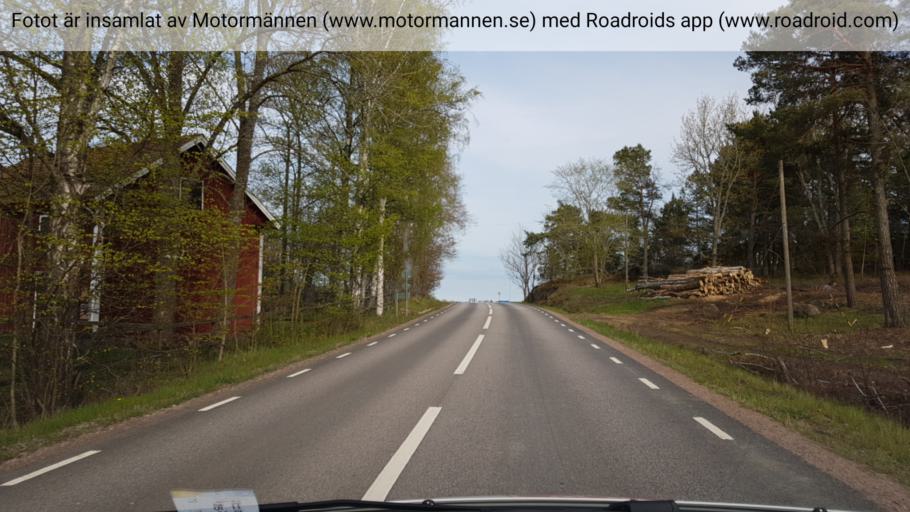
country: SE
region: Kalmar
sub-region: Vasterviks Kommun
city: Forserum
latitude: 57.9389
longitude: 16.4594
